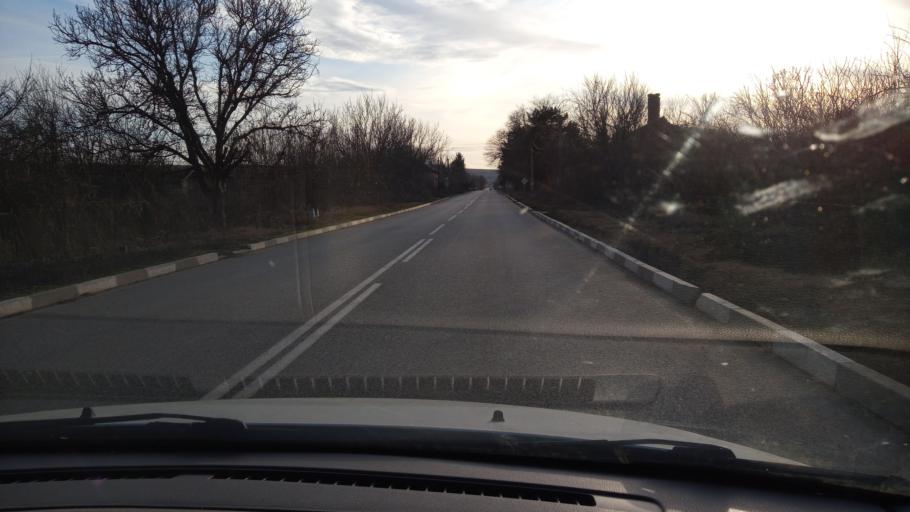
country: BG
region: Pleven
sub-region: Obshtina Pleven
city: Slavyanovo
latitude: 43.5561
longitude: 24.8664
